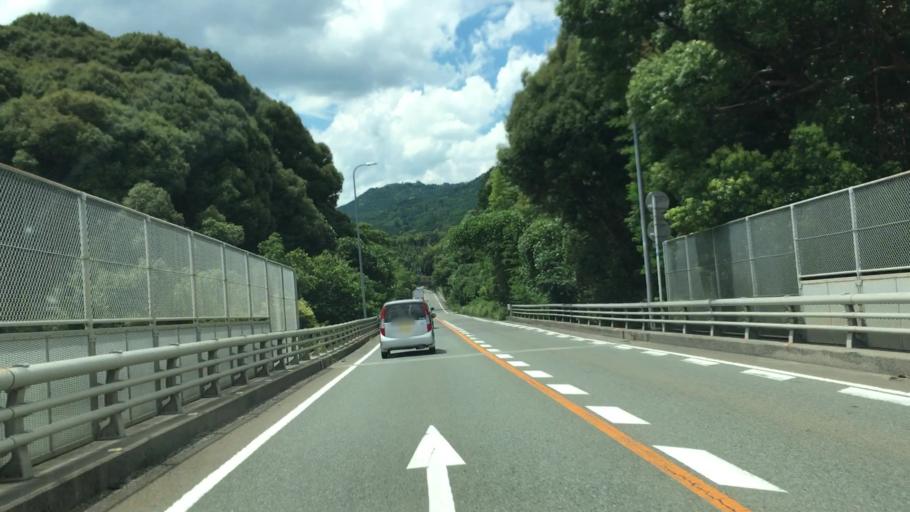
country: JP
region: Fukuoka
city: Chikushino-shi
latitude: 33.4446
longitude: 130.5362
